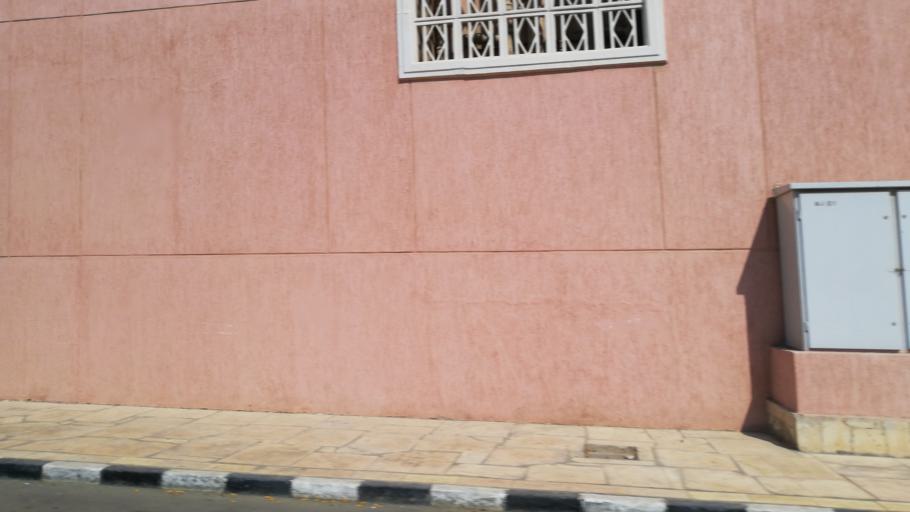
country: EG
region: Muhafazat al Qalyubiyah
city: Al Khankah
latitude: 30.0618
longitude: 31.4878
